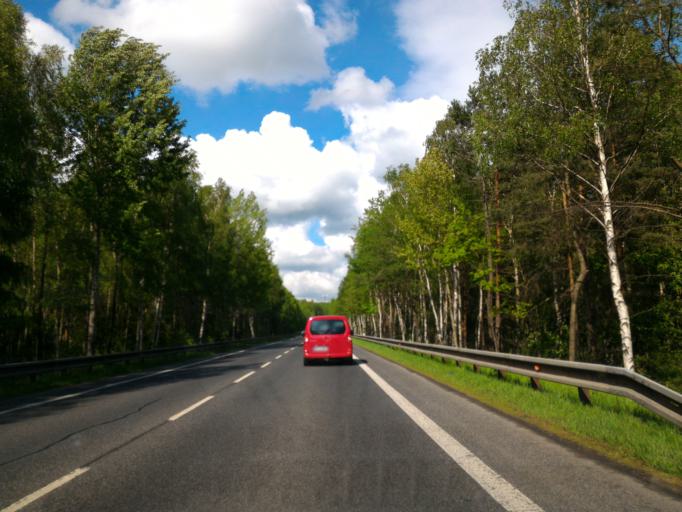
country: CZ
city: Novy Bor
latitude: 50.7844
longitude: 14.5894
